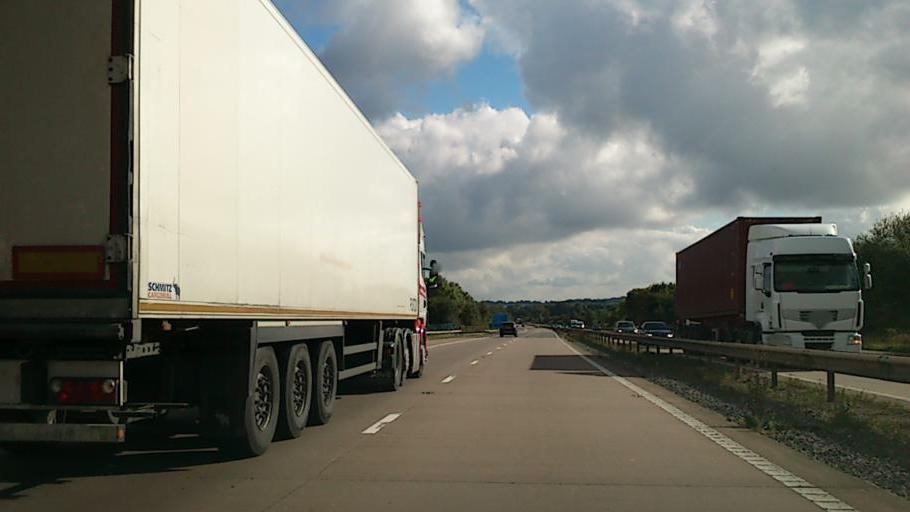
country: GB
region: England
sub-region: Staffordshire
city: Brewood
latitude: 52.6420
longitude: -2.1643
